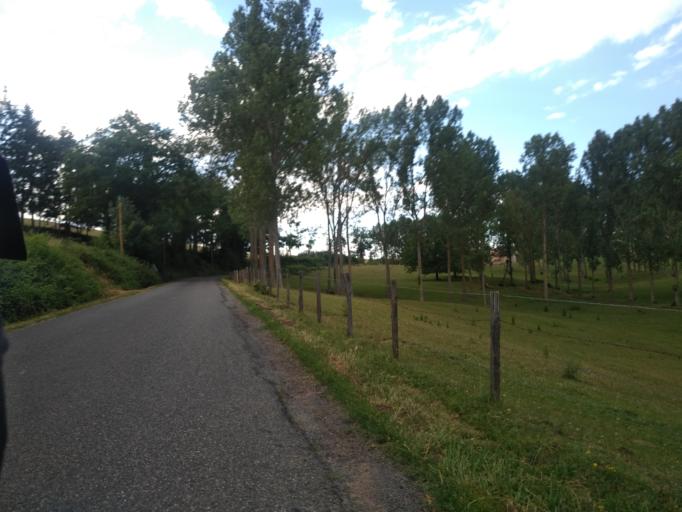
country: FR
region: Rhone-Alpes
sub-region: Departement de la Loire
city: Panissieres
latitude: 45.7427
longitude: 4.3502
